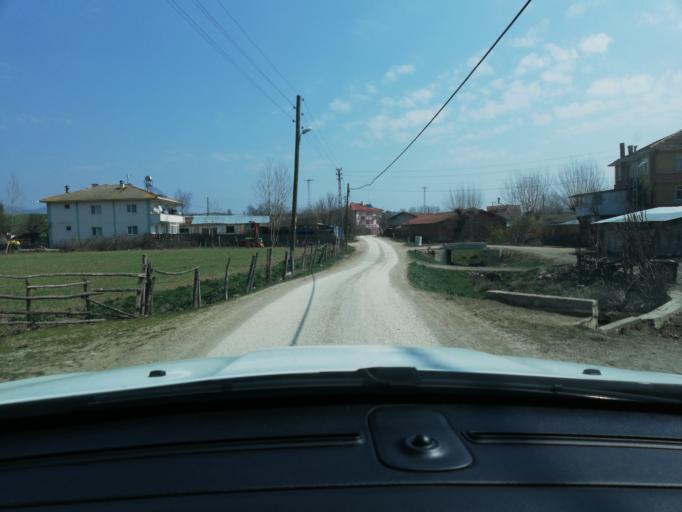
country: TR
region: Kastamonu
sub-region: Cide
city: Kastamonu
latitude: 41.4583
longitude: 33.7618
